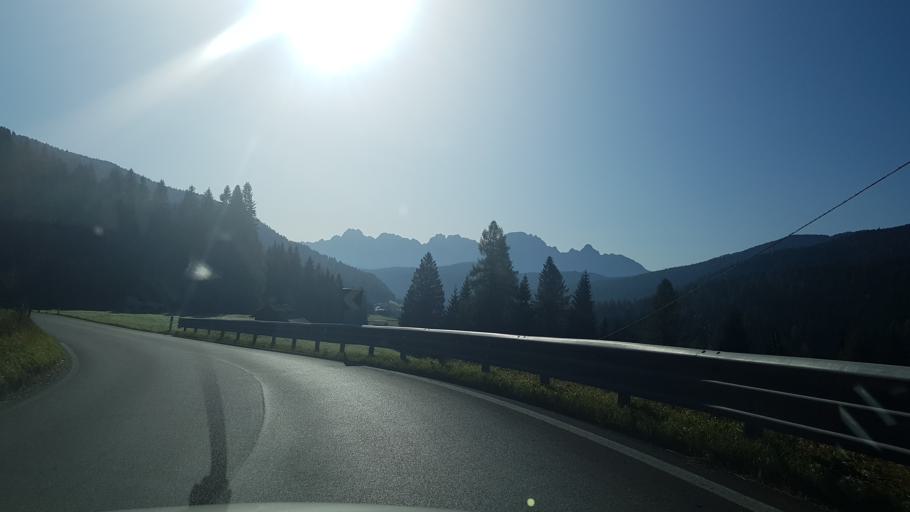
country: IT
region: Veneto
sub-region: Provincia di Belluno
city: Candide
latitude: 46.6226
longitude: 12.4707
